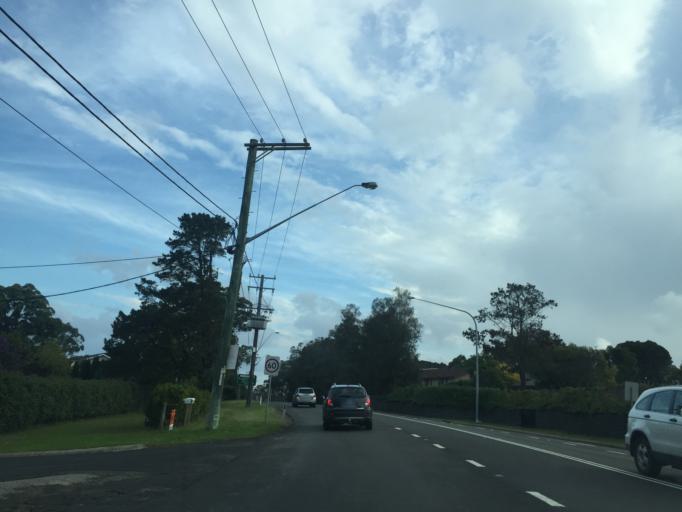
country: AU
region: New South Wales
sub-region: Hornsby Shire
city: Galston
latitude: -33.6791
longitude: 151.0298
